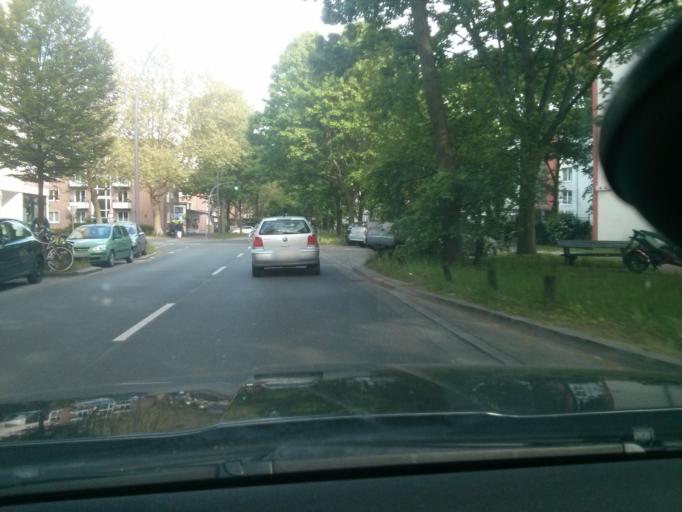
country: DE
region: Hamburg
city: Stellingen
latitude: 53.5751
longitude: 9.9457
